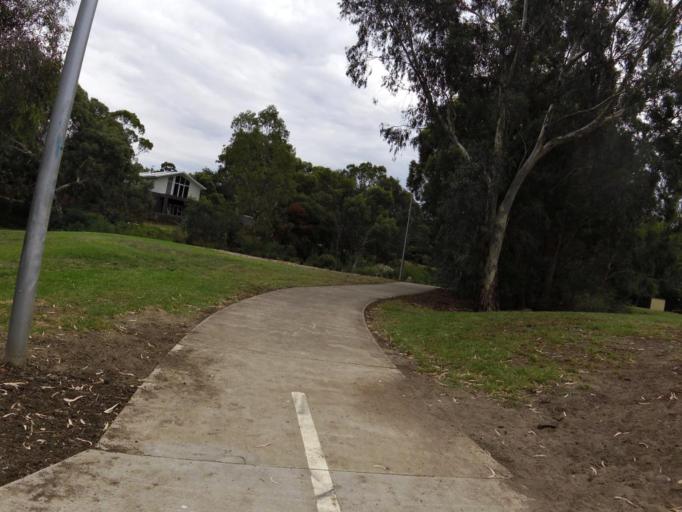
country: AU
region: Victoria
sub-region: Moonee Valley
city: Essendon West
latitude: -37.7472
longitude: 144.8811
